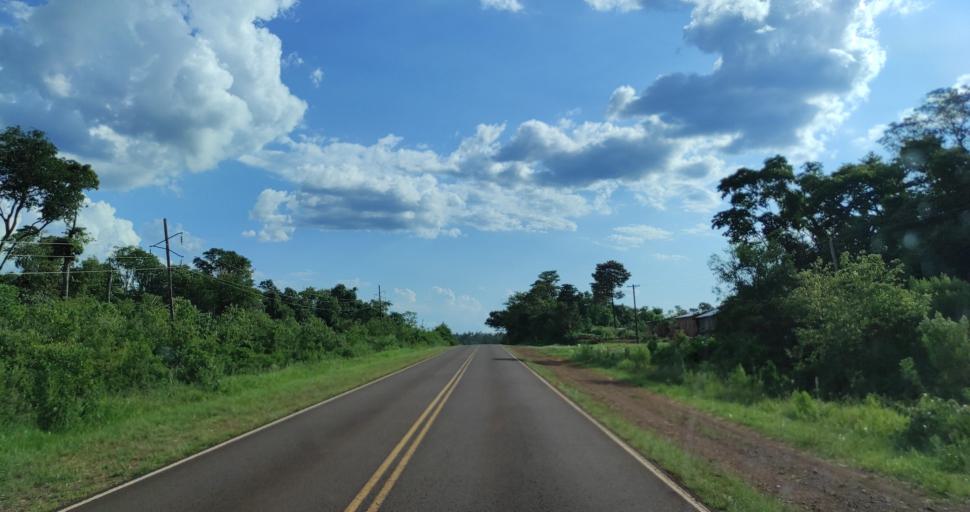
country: AR
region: Misiones
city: San Vicente
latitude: -26.3533
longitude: -54.2110
